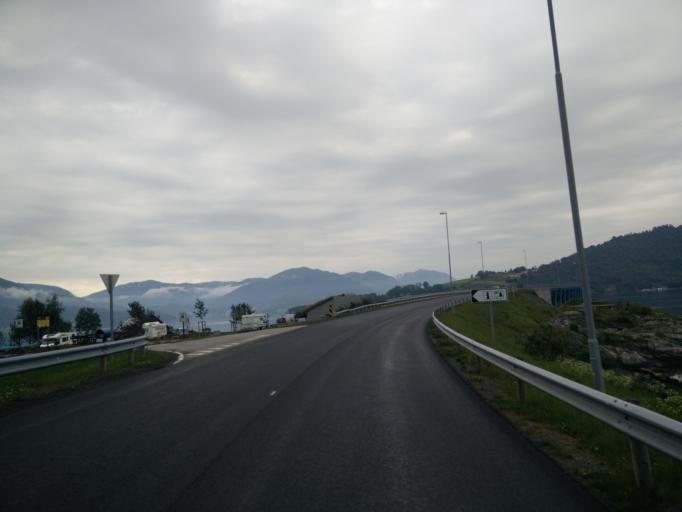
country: NO
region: More og Romsdal
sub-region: Kristiansund
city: Rensvik
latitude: 62.9904
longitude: 7.8827
